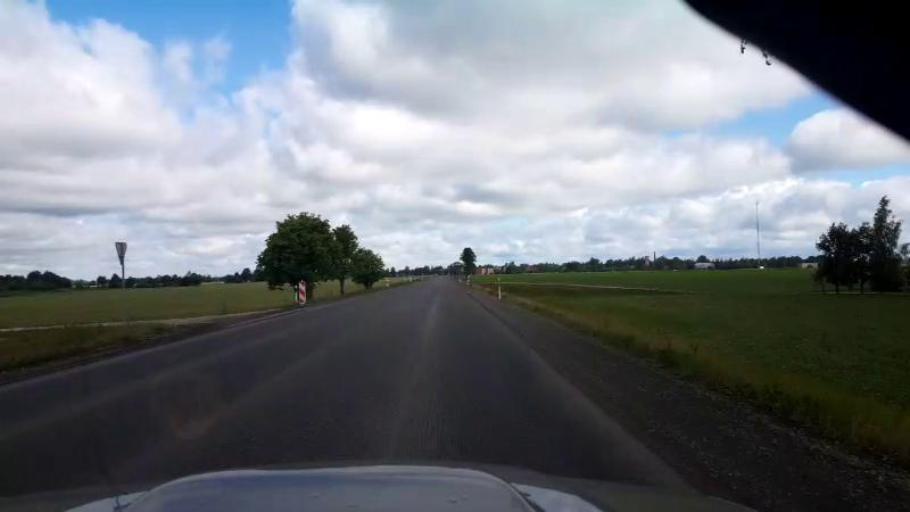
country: LV
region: Bauskas Rajons
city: Bauska
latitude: 56.3023
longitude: 24.3425
